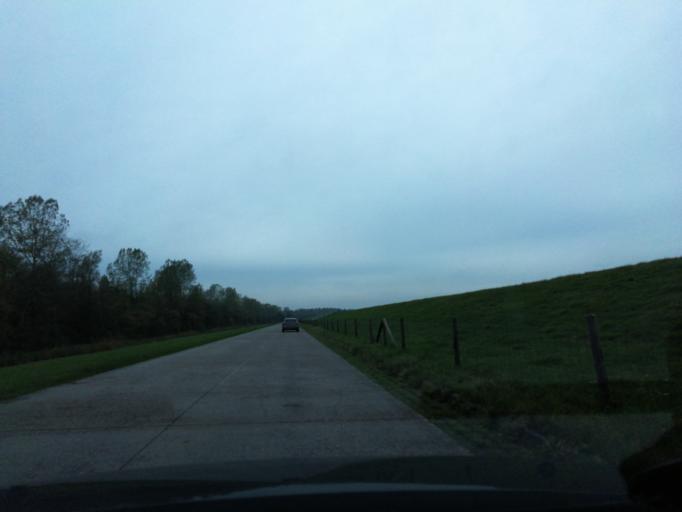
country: DE
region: Lower Saxony
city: Schillig
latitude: 53.6405
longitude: 8.0579
